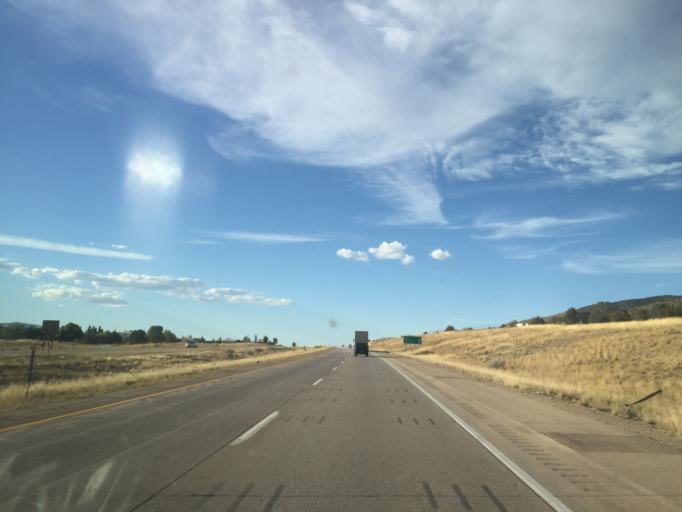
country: US
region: Utah
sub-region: Juab County
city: Nephi
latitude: 39.7234
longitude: -111.8200
